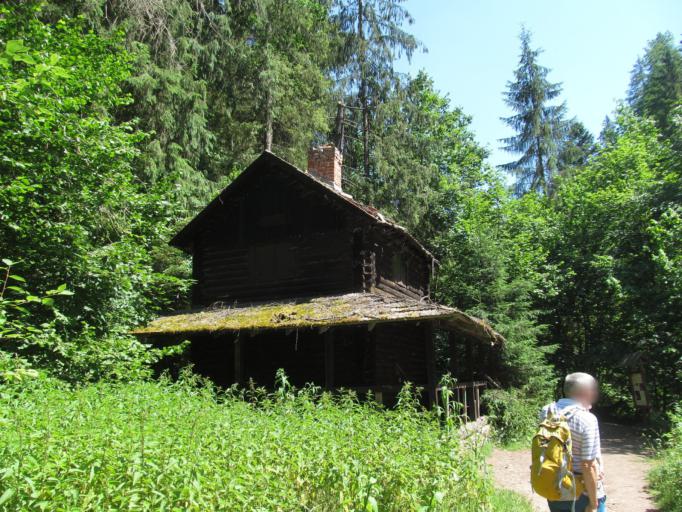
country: SK
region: Kosicky
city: Dobsina
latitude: 48.9582
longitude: 20.4044
